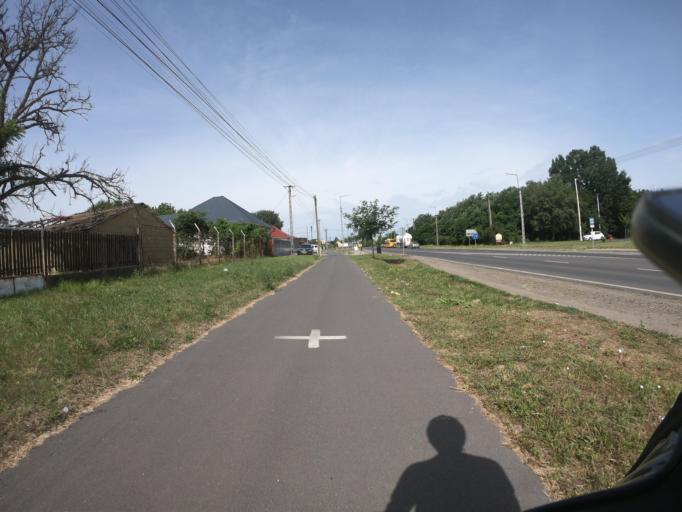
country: HU
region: Jasz-Nagykun-Szolnok
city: Tiszafured
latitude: 47.6073
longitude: 20.7643
